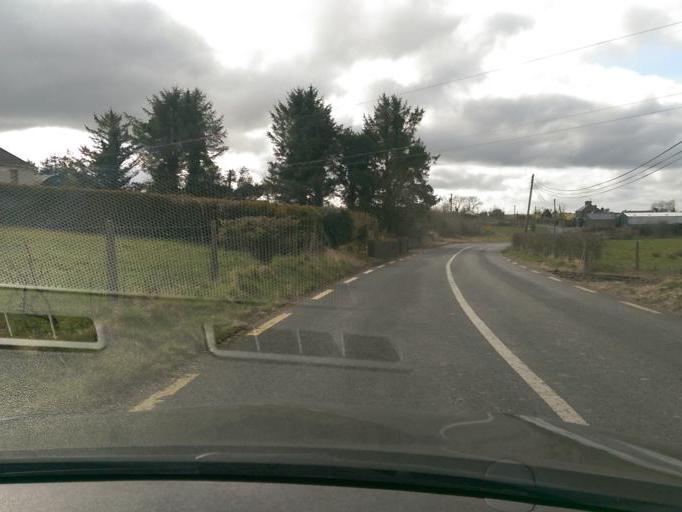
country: IE
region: Connaught
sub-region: County Galway
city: Loughrea
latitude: 53.3258
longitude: -8.4180
